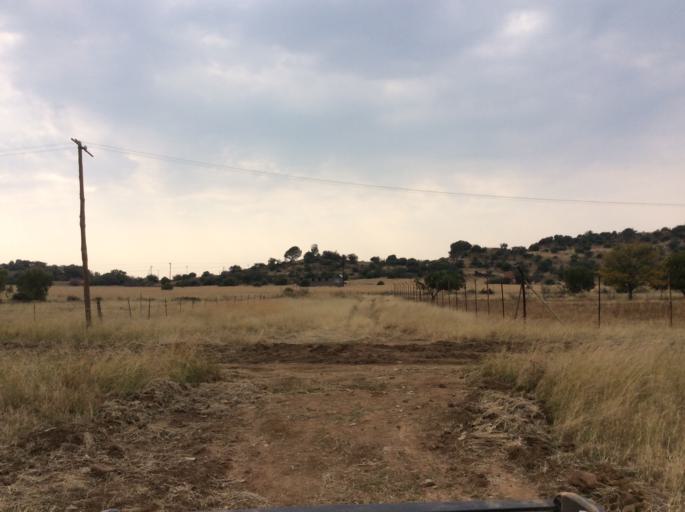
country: LS
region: Mafeteng
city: Mafeteng
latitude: -29.9891
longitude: 27.0196
